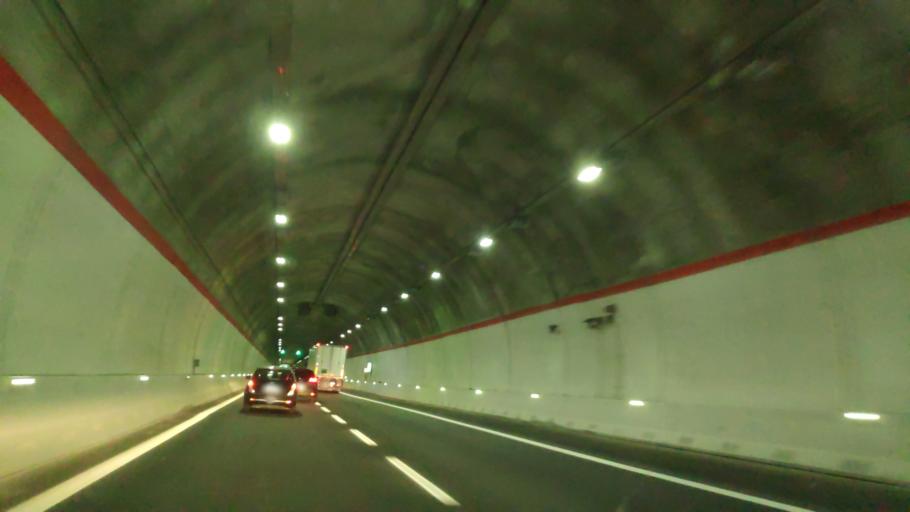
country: IT
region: Basilicate
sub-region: Provincia di Potenza
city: Lagonegro
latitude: 40.1406
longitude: 15.7573
